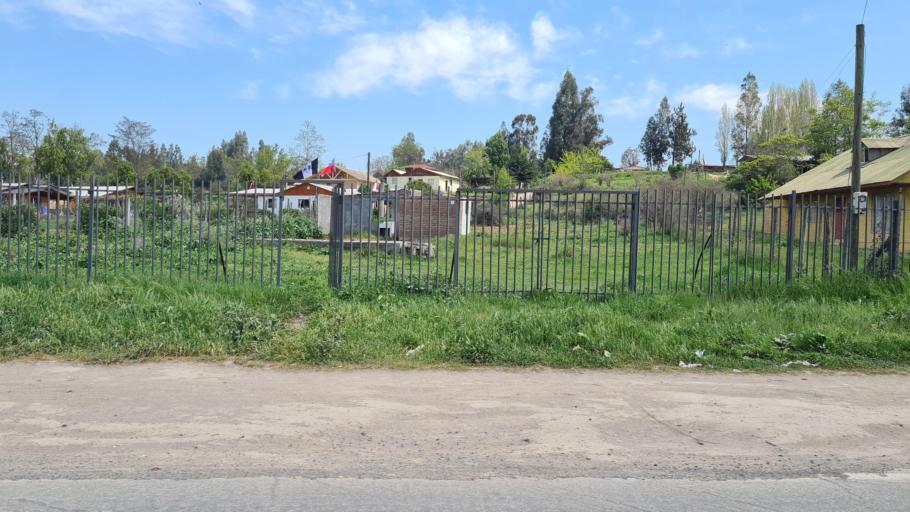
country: CL
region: O'Higgins
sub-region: Provincia de Cachapoal
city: San Vicente
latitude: -34.1668
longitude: -71.4082
